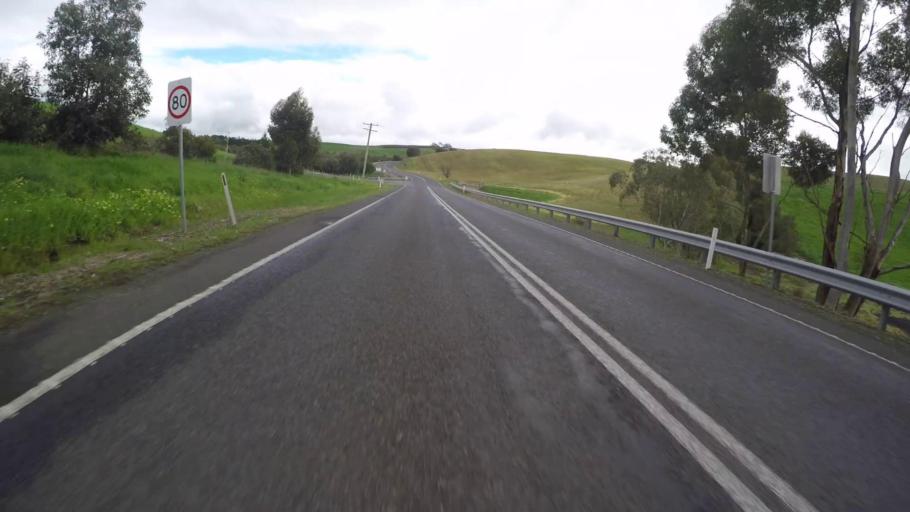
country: AU
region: Victoria
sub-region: Greater Geelong
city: Wandana Heights
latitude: -38.1703
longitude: 144.2393
